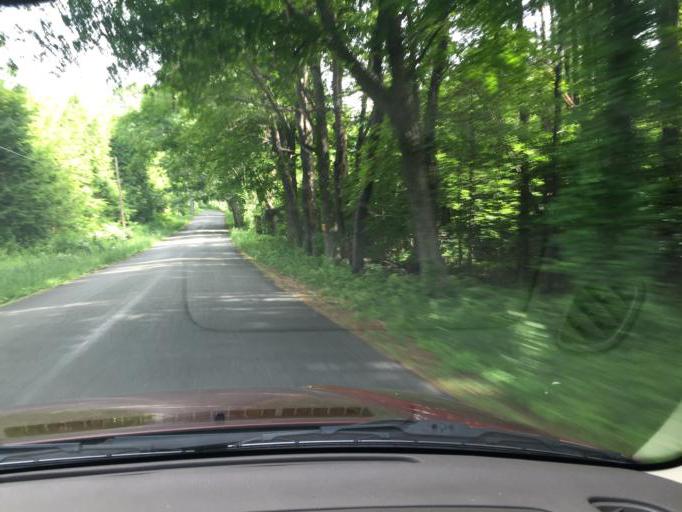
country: US
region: Connecticut
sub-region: Litchfield County
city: Litchfield
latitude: 41.7900
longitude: -73.2592
